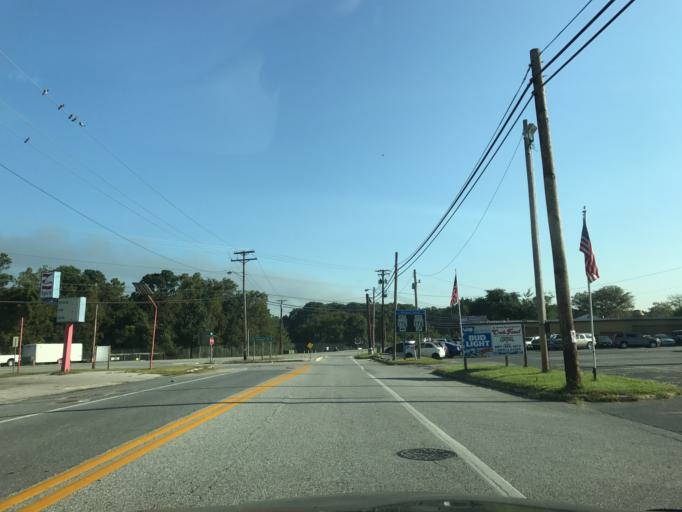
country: US
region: Maryland
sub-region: Anne Arundel County
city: Severn
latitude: 39.1596
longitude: -76.6834
